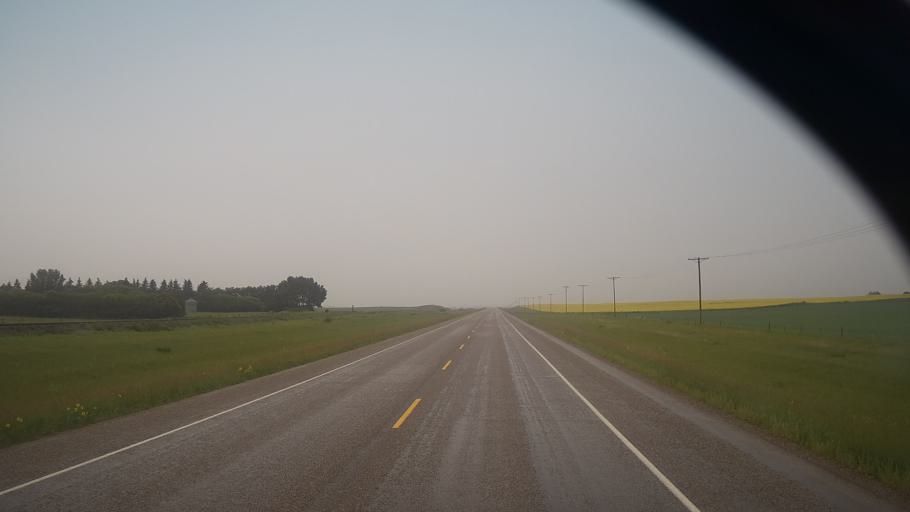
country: CA
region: Saskatchewan
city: Biggar
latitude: 52.1380
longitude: -108.1770
